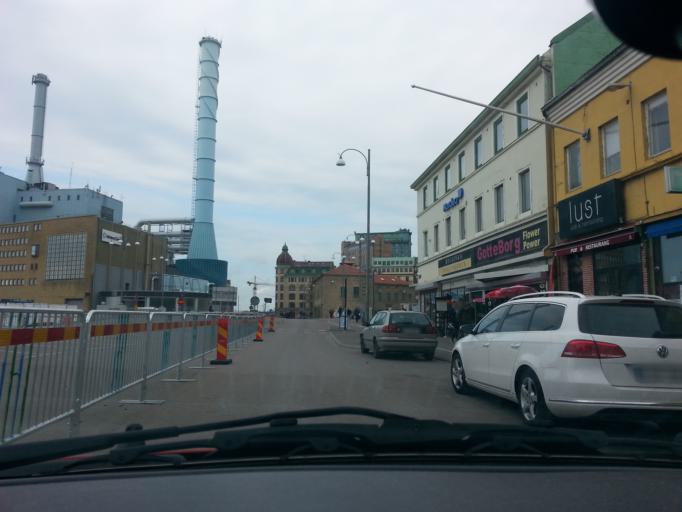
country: SE
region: Vaestra Goetaland
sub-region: Goteborg
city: Goeteborg
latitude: 57.7012
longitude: 11.9544
